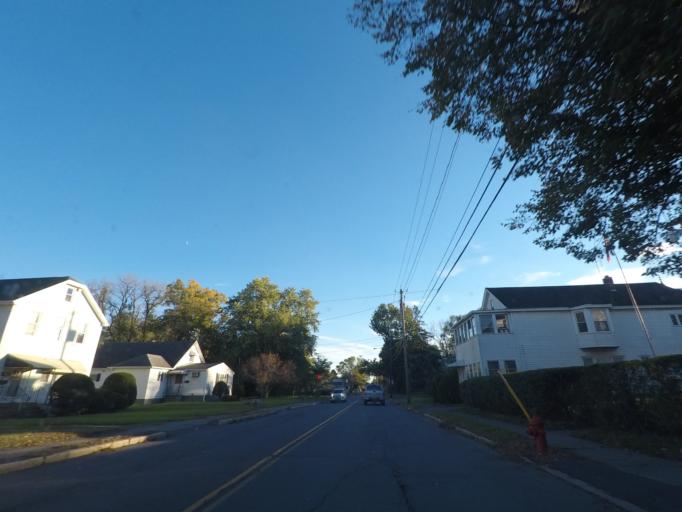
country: US
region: New York
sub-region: Albany County
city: Green Island
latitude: 42.7555
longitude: -73.7005
